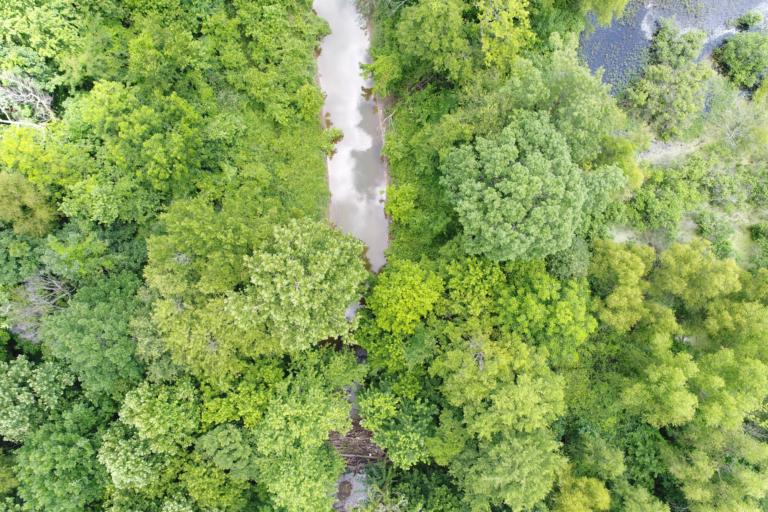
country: US
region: Mississippi
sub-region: De Soto County
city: Walls
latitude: 34.9182
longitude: -90.1990
